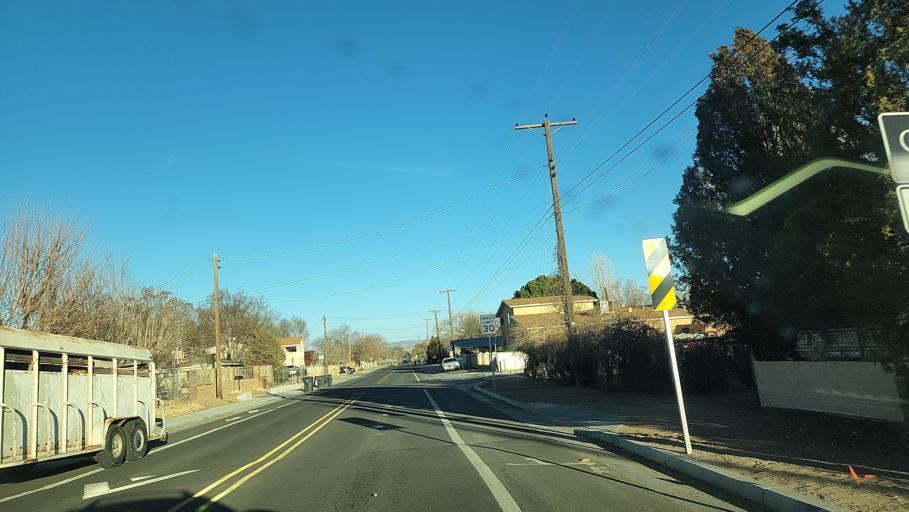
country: US
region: New Mexico
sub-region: Bernalillo County
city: South Valley
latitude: 35.0305
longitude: -106.7009
